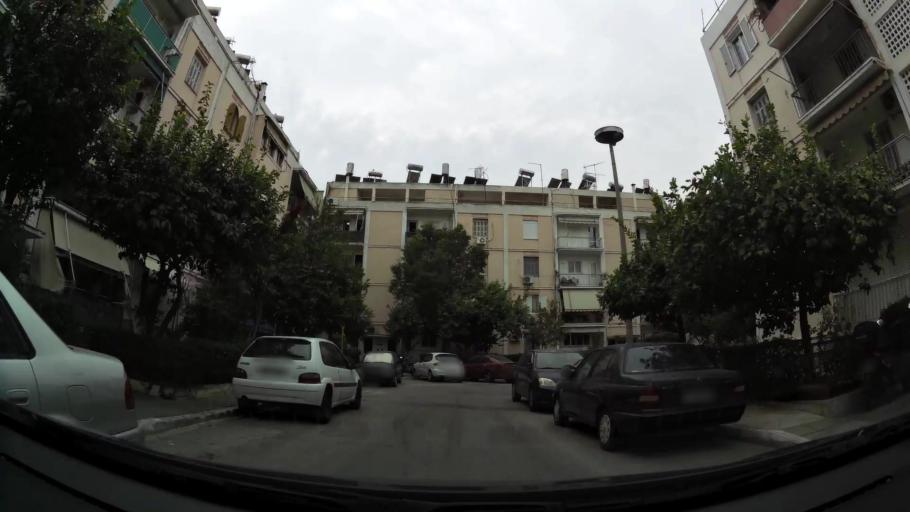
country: GR
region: Attica
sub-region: Nomarchia Athinas
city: Aigaleo
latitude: 37.9755
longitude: 23.6822
